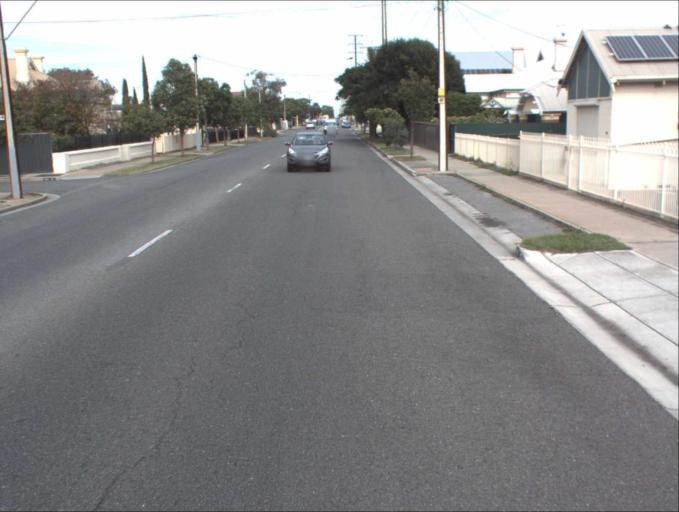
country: AU
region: South Australia
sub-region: Port Adelaide Enfield
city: Birkenhead
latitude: -34.8353
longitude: 138.4854
